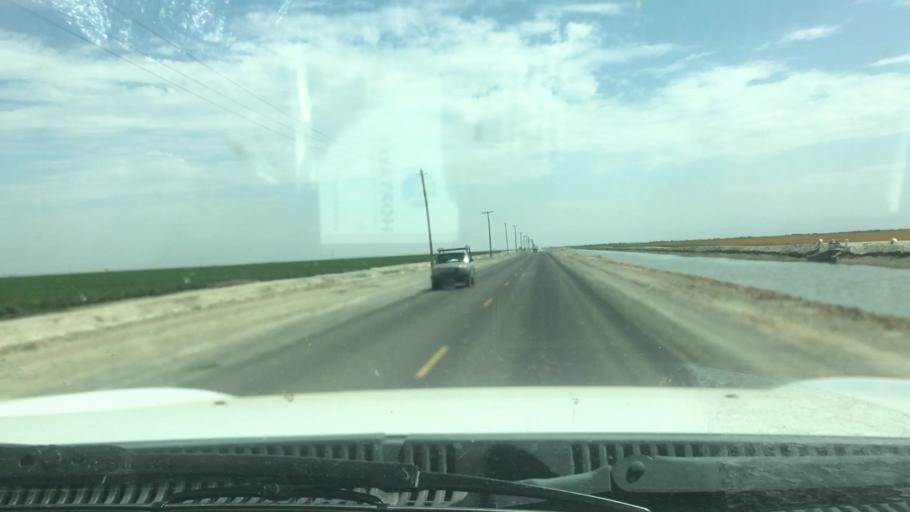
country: US
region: California
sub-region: Tulare County
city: Alpaugh
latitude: 35.8848
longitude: -119.5735
